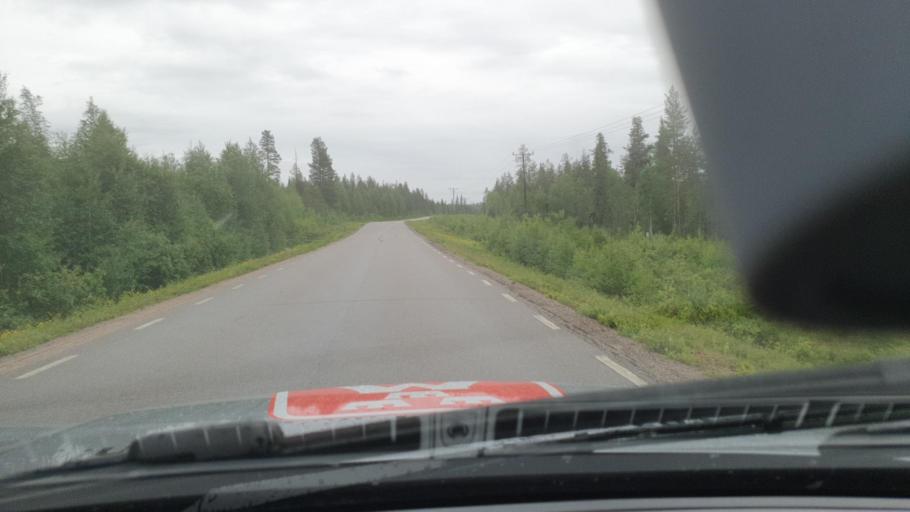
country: SE
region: Norrbotten
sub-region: Pajala Kommun
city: Pajala
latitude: 66.7815
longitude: 23.1357
